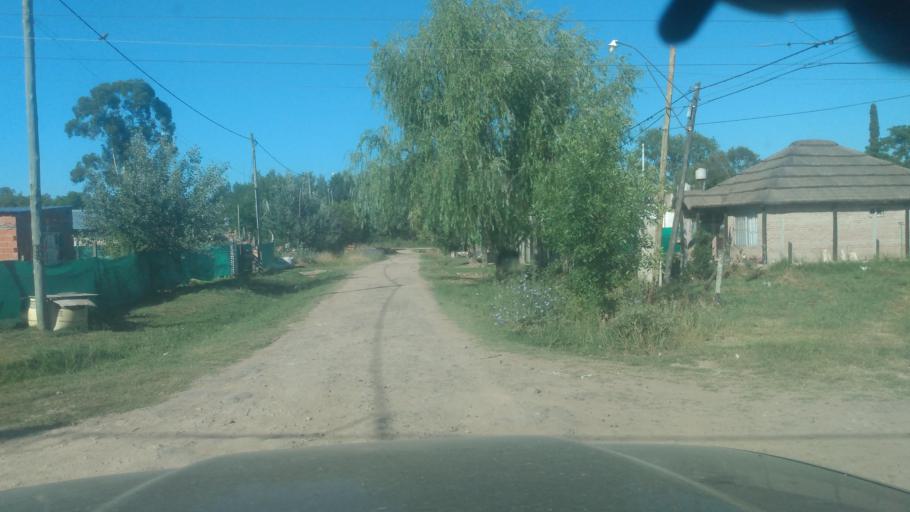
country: AR
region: Buenos Aires
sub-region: Partido de Lujan
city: Lujan
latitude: -34.5872
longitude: -59.0603
